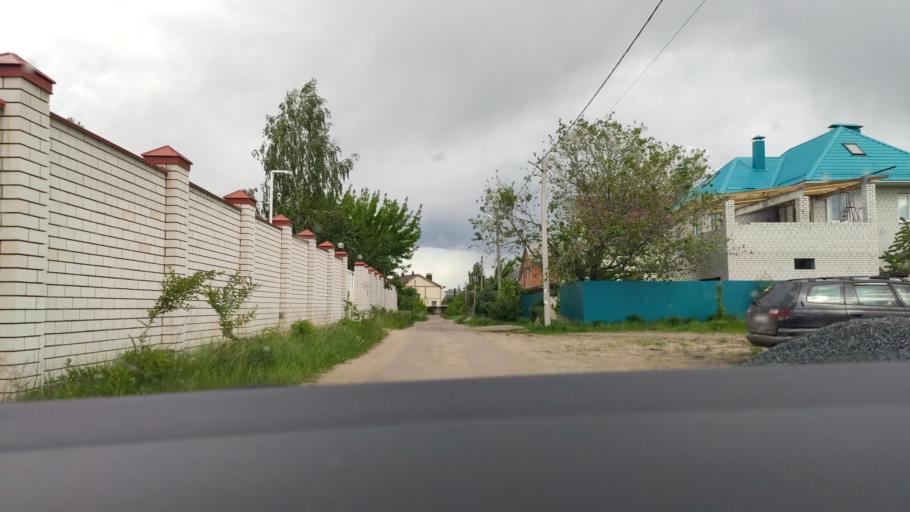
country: RU
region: Voronezj
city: Somovo
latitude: 51.6810
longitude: 39.3142
